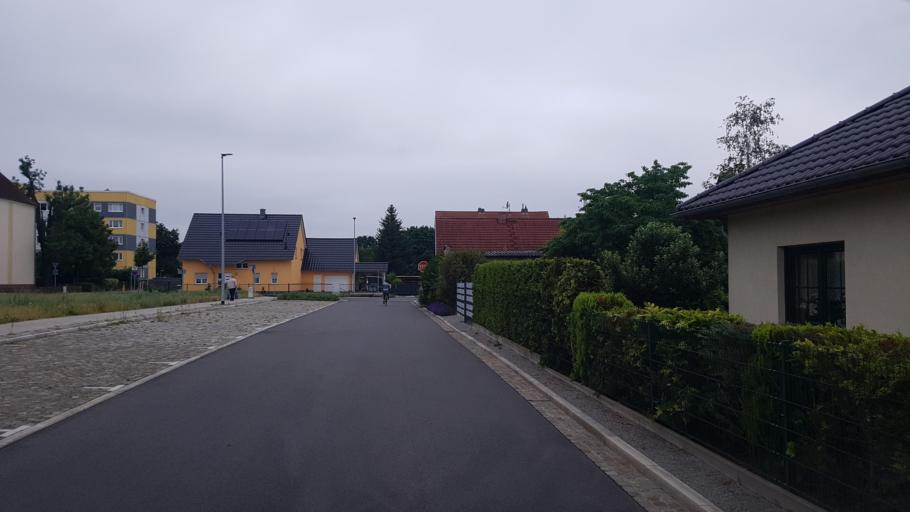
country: DE
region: Brandenburg
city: Senftenberg
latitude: 51.5215
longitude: 13.9991
